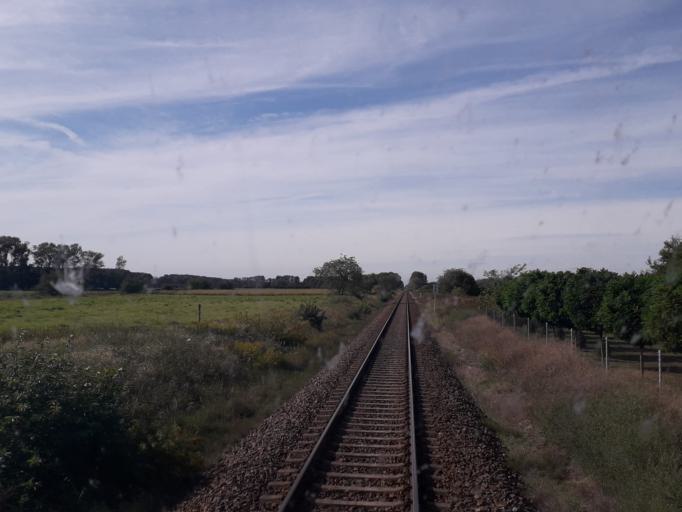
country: DE
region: Brandenburg
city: Kremmen
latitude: 52.8047
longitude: 13.0208
